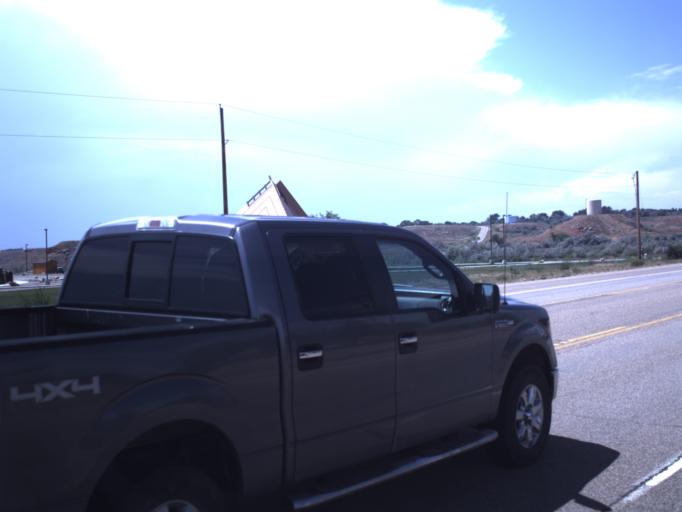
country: US
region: Utah
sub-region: Duchesne County
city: Roosevelt
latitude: 40.3020
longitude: -109.8788
